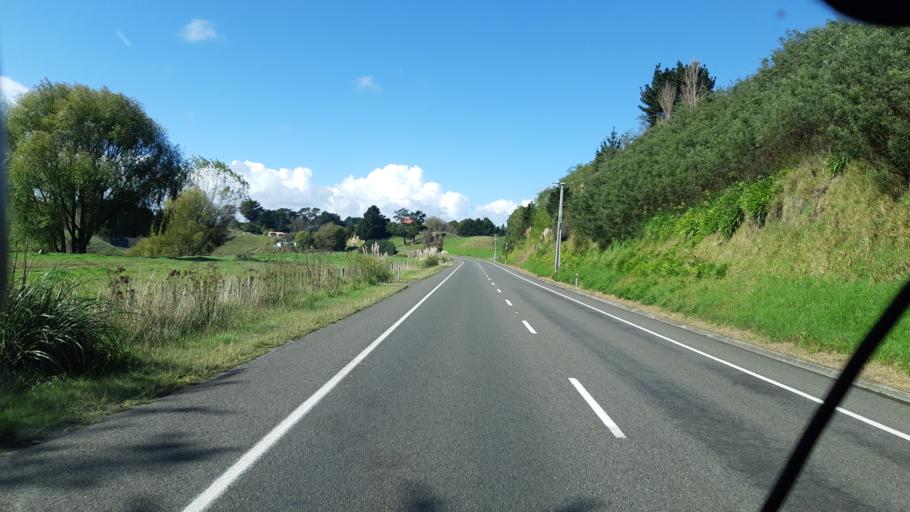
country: NZ
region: Manawatu-Wanganui
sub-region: Wanganui District
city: Wanganui
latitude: -39.9570
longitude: 175.0724
